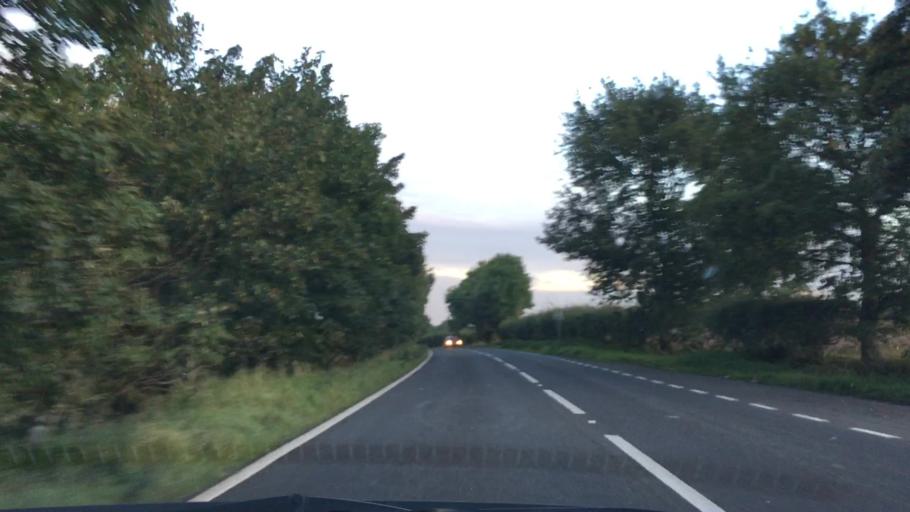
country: GB
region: England
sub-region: North East Lincolnshire
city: Wold Newton
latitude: 53.4771
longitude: -0.1183
